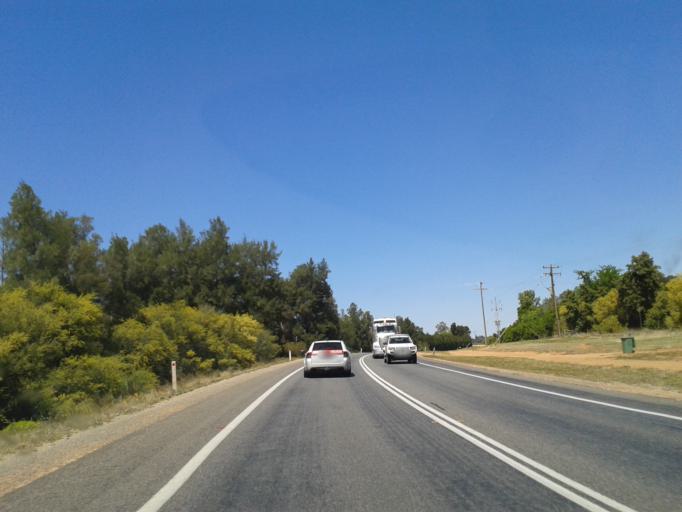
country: AU
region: New South Wales
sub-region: Wentworth
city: Gol Gol
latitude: -34.2078
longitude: 142.2487
